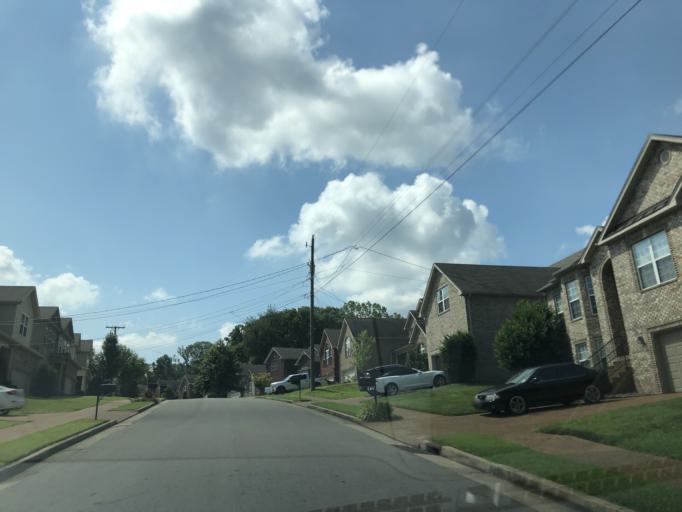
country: US
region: Tennessee
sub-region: Williamson County
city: Nolensville
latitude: 36.0101
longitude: -86.6851
